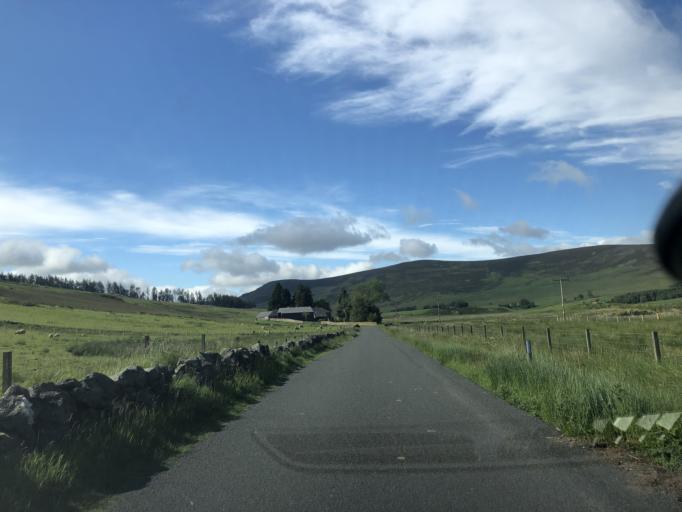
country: GB
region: Scotland
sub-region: Angus
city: Kirriemuir
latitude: 56.8094
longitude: -3.0341
